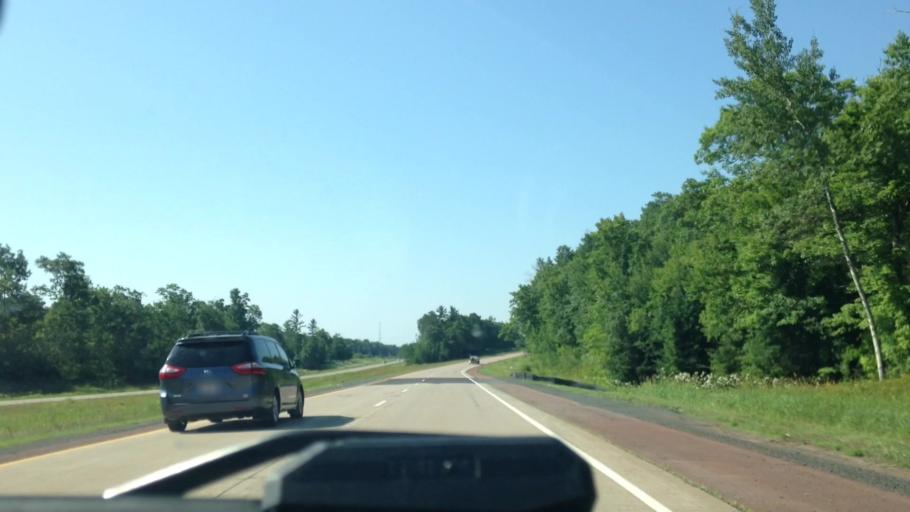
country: US
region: Wisconsin
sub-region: Douglas County
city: Lake Nebagamon
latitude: 46.3936
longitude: -91.8190
